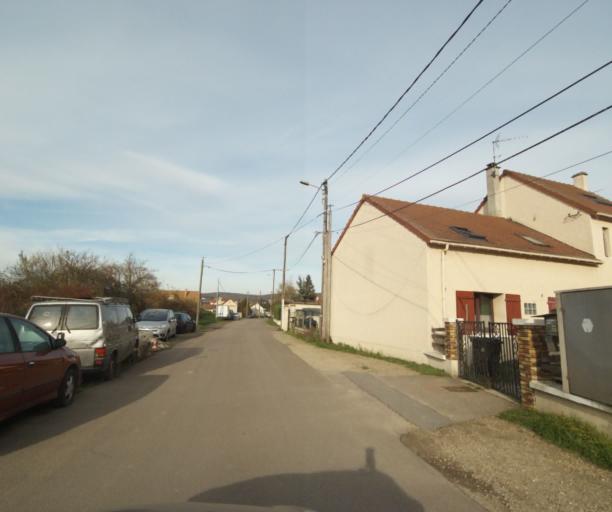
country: FR
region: Ile-de-France
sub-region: Departement des Yvelines
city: Triel-sur-Seine
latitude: 48.9685
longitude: 2.0067
